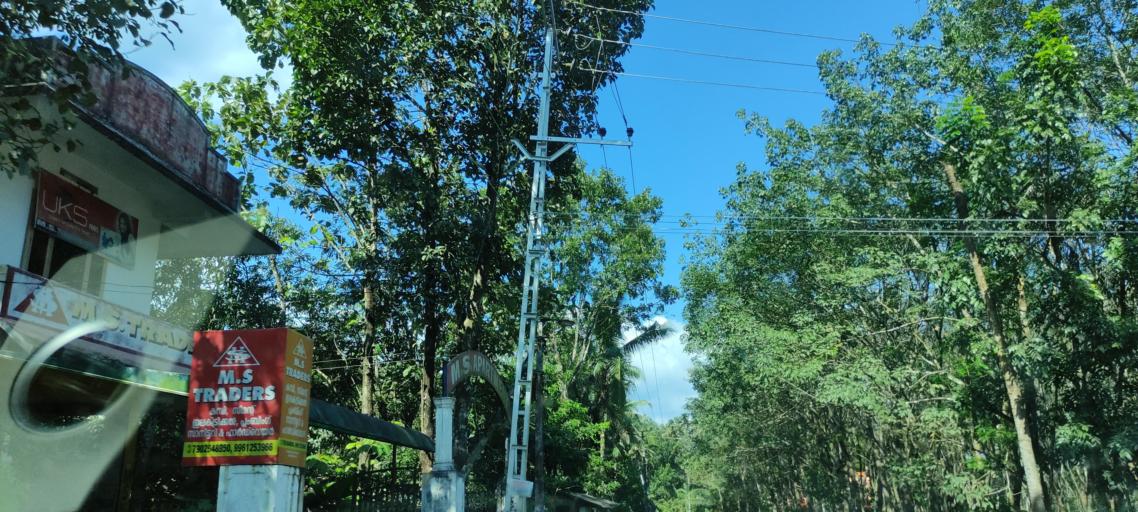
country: IN
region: Kerala
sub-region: Pattanamtitta
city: Adur
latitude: 9.1899
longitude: 76.7451
